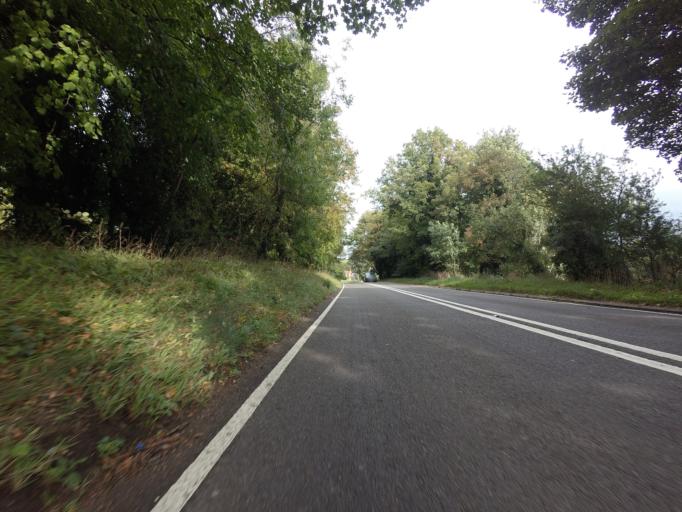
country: GB
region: England
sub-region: Essex
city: Saffron Walden
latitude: 52.0195
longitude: 0.2136
